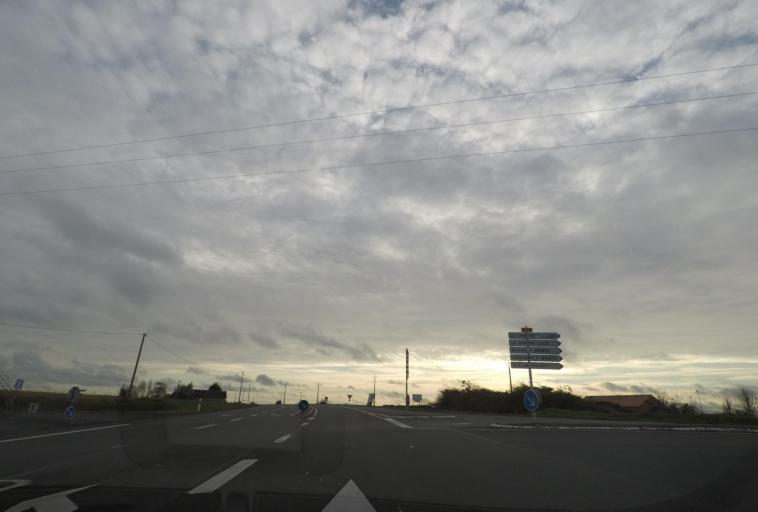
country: FR
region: Pays de la Loire
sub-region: Departement de la Sarthe
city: Saint-Calais
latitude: 47.9195
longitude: 0.7658
